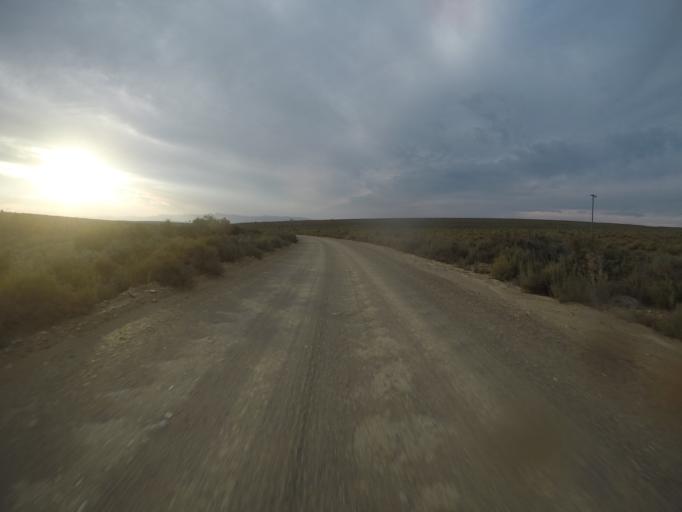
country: ZA
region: Eastern Cape
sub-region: Cacadu District Municipality
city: Willowmore
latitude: -33.5811
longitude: 23.1805
